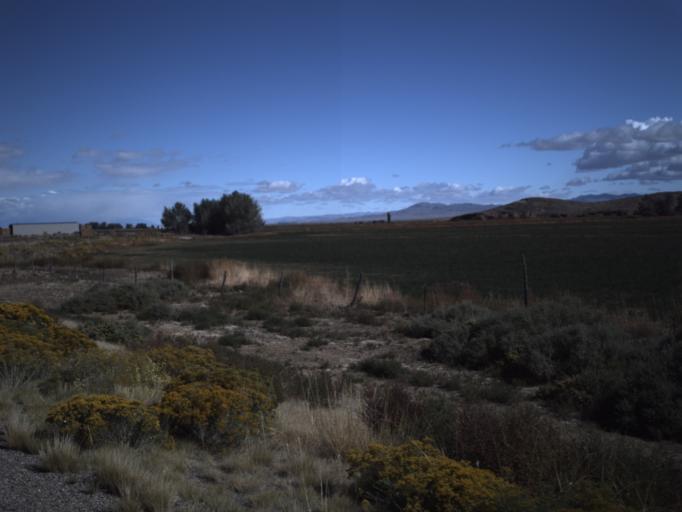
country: US
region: Nevada
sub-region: White Pine County
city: McGill
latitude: 38.9170
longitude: -114.0282
